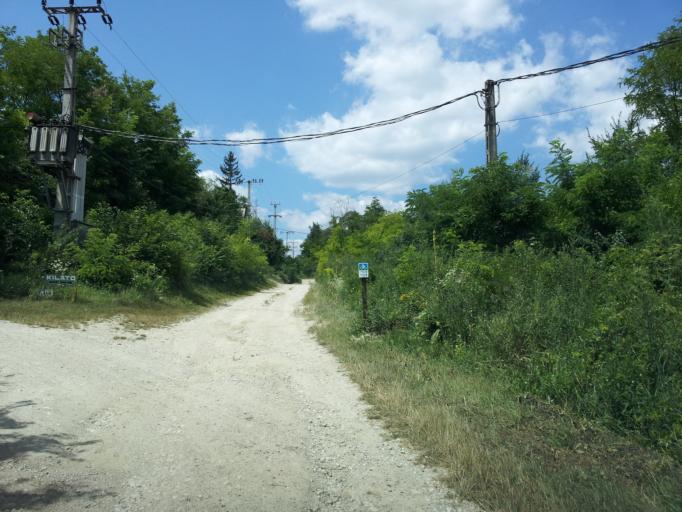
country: HU
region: Veszprem
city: Balatonkenese
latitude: 47.0409
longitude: 18.0929
